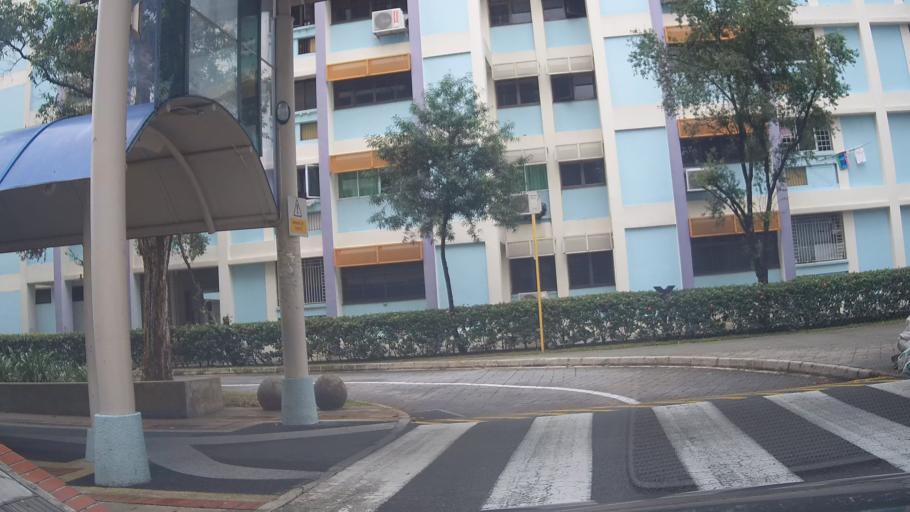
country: MY
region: Johor
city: Johor Bahru
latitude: 1.4416
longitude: 103.7998
